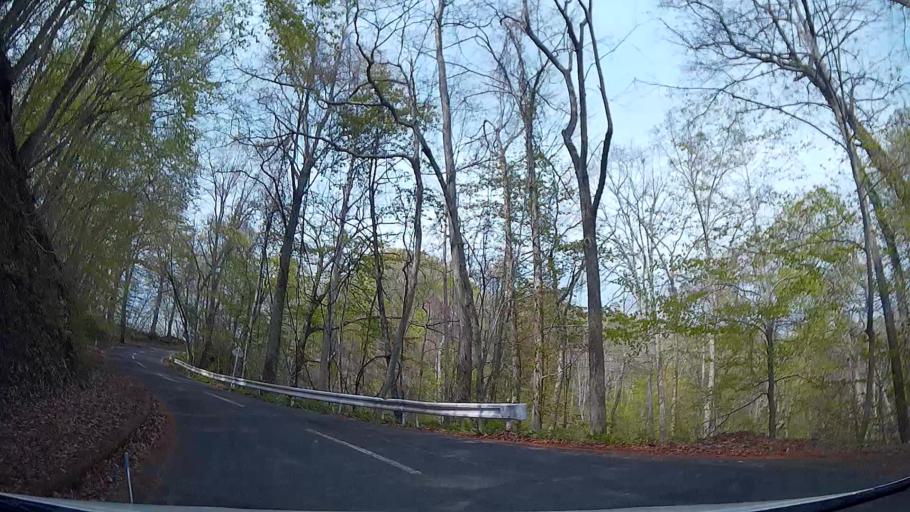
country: JP
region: Akita
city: Hanawa
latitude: 40.4374
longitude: 140.9168
